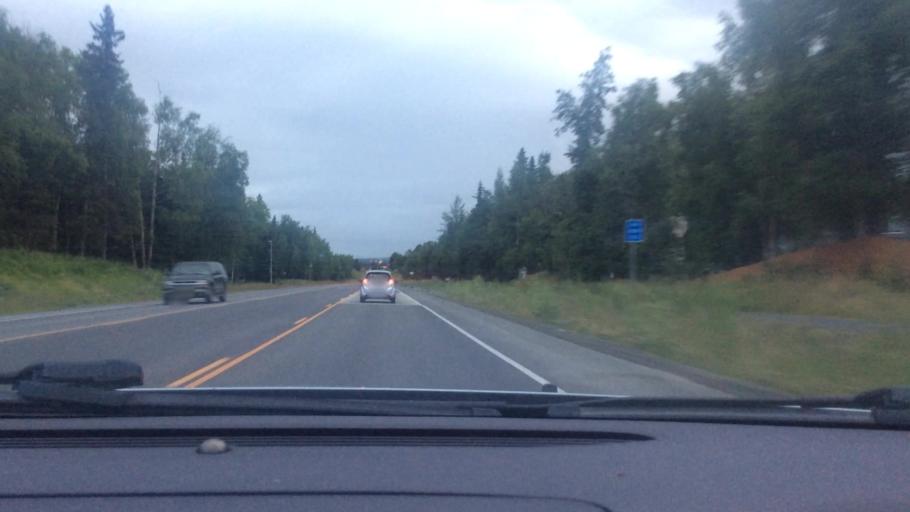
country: US
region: Alaska
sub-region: Anchorage Municipality
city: Anchorage
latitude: 61.1375
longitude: -149.8095
